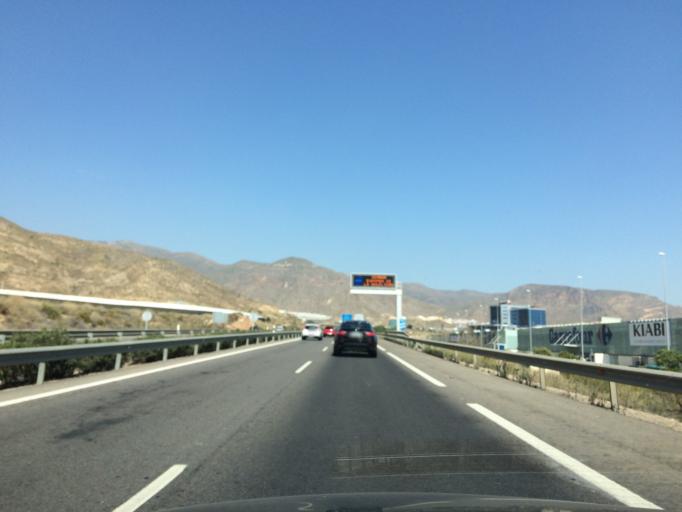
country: ES
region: Andalusia
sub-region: Provincia de Almeria
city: Aguadulce
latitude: 36.8158
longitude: -2.6041
